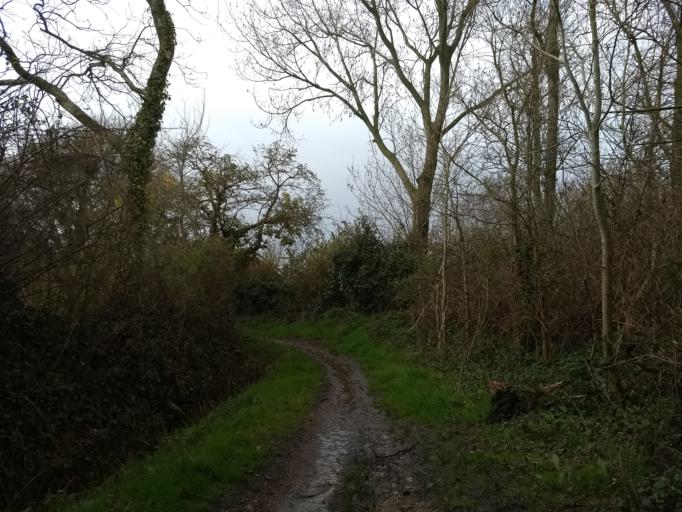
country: GB
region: England
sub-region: Isle of Wight
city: Ryde
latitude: 50.7207
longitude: -1.1887
